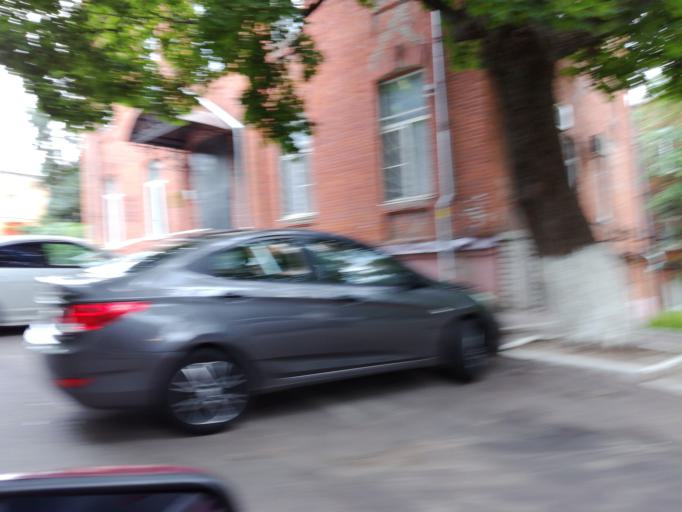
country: RU
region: Kursk
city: Kursk
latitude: 51.7422
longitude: 36.1842
